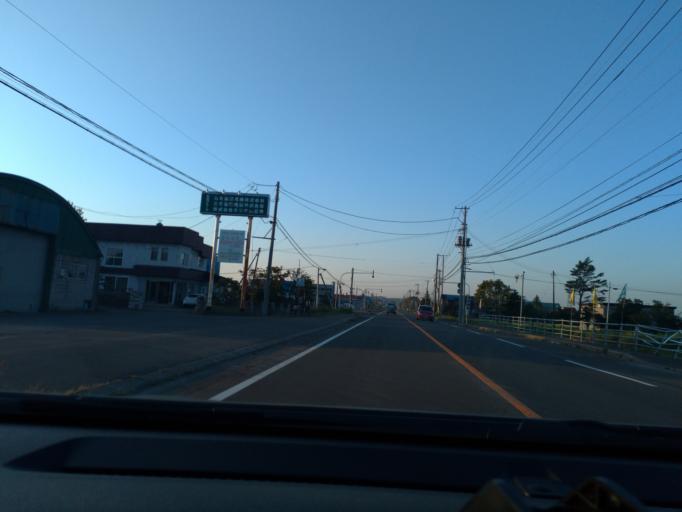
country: JP
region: Hokkaido
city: Tobetsu
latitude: 43.2041
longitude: 141.5206
